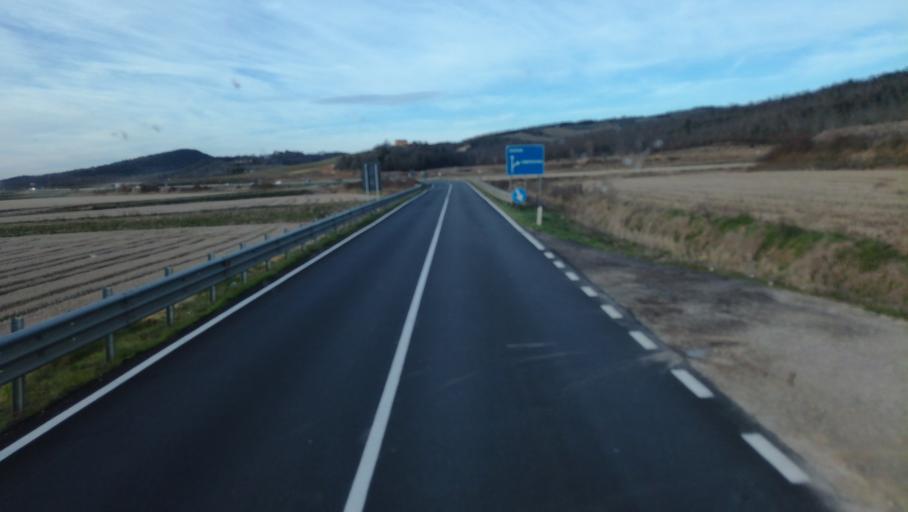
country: IT
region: Tuscany
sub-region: Provincia di Siena
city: Murlo
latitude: 43.1555
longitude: 11.2902
